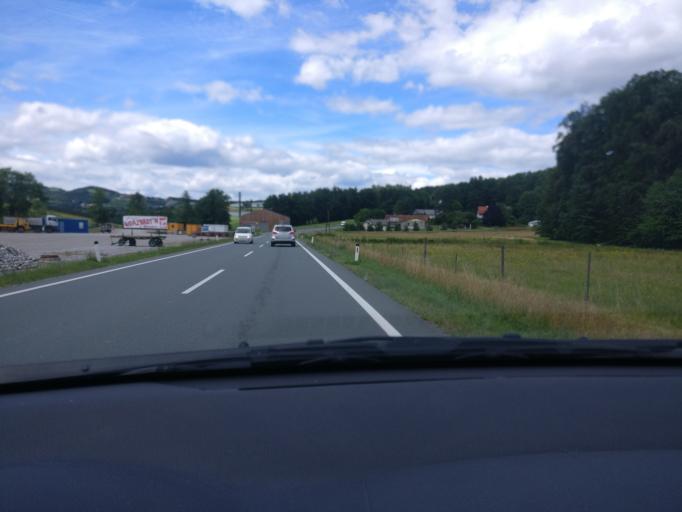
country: AT
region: Styria
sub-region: Politischer Bezirk Weiz
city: Hirnsdorf
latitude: 47.1787
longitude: 15.8102
